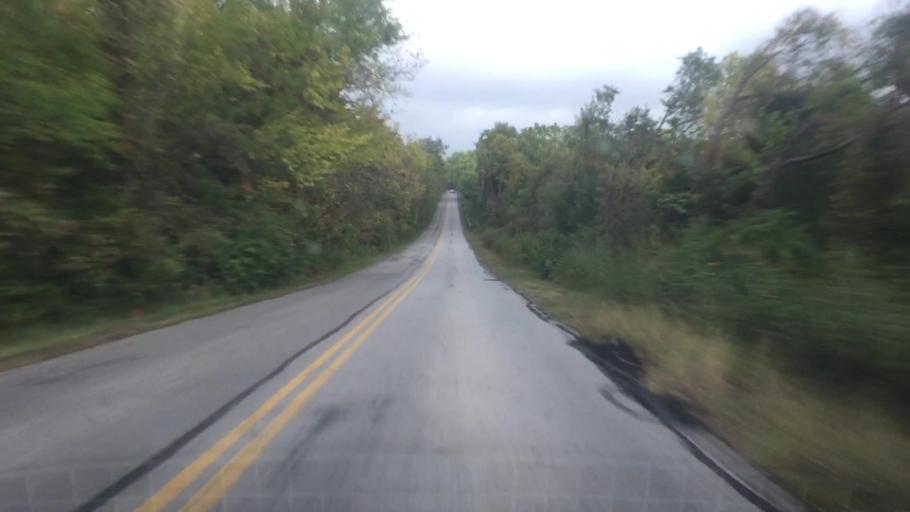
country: US
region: Kansas
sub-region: Johnson County
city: Shawnee
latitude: 39.0475
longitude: -94.7618
